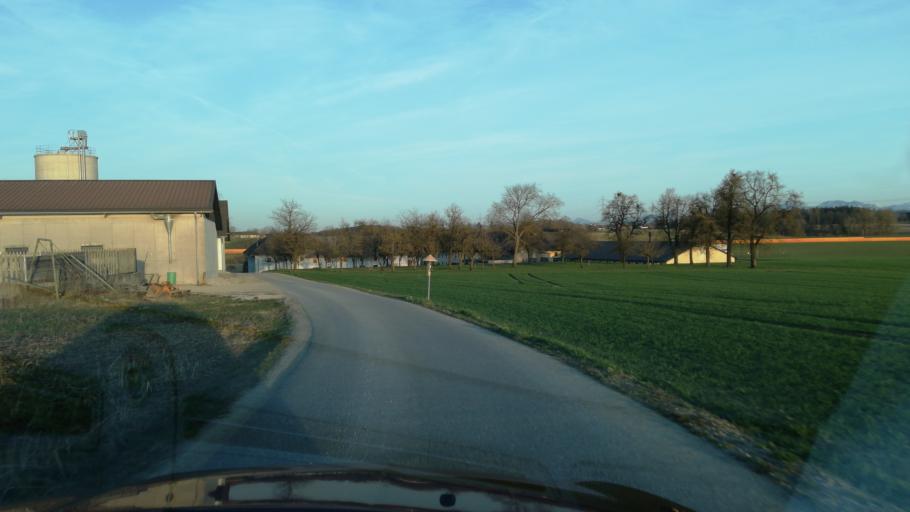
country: AT
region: Upper Austria
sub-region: Wels-Land
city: Sattledt
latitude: 48.0917
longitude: 14.0628
